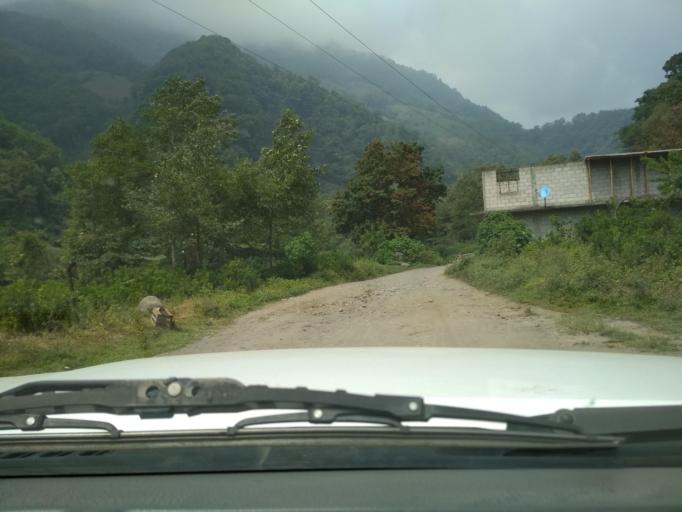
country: MX
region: Veracruz
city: Xocotla
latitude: 18.9892
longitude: -97.1114
